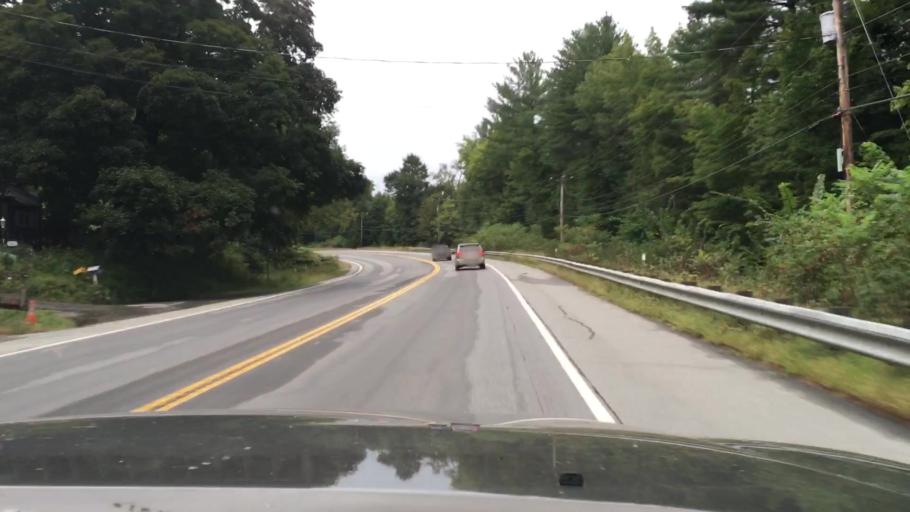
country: US
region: New Hampshire
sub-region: Cheshire County
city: Chesterfield
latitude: 42.8976
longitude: -72.5157
